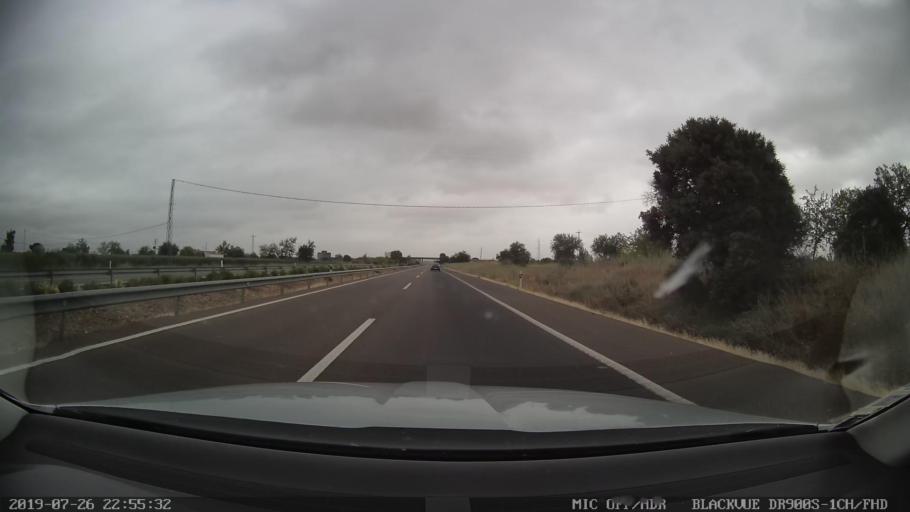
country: ES
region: Extremadura
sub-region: Provincia de Badajoz
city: Arroyo de San Servan
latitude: 38.8877
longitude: -6.4330
